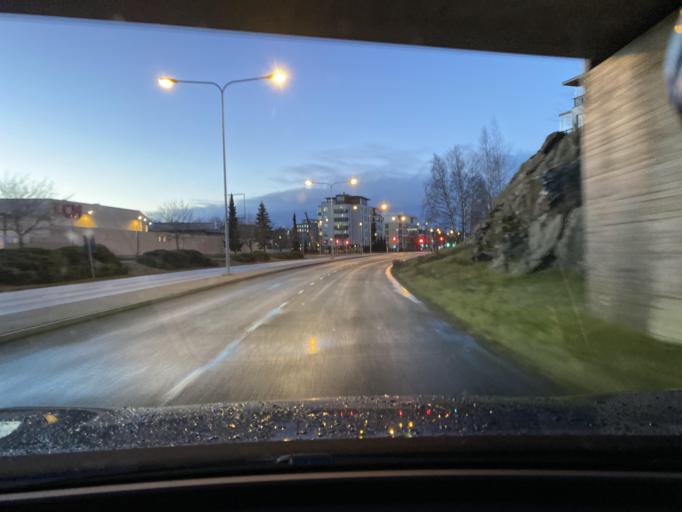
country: FI
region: Satakunta
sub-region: Rauma
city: Rauma
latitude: 61.1339
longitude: 21.5051
